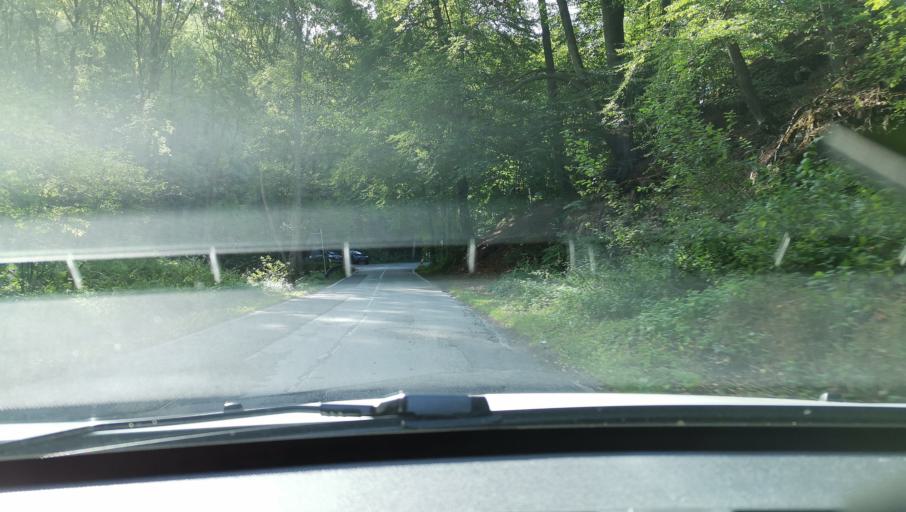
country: DE
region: North Rhine-Westphalia
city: Ennepetal
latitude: 51.3247
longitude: 7.3920
